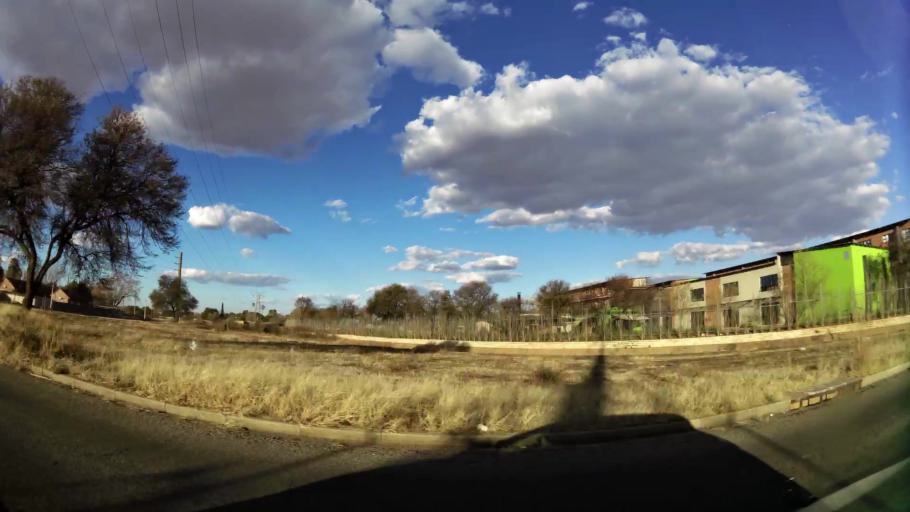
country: ZA
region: North-West
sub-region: Dr Kenneth Kaunda District Municipality
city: Potchefstroom
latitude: -26.7047
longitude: 27.0856
